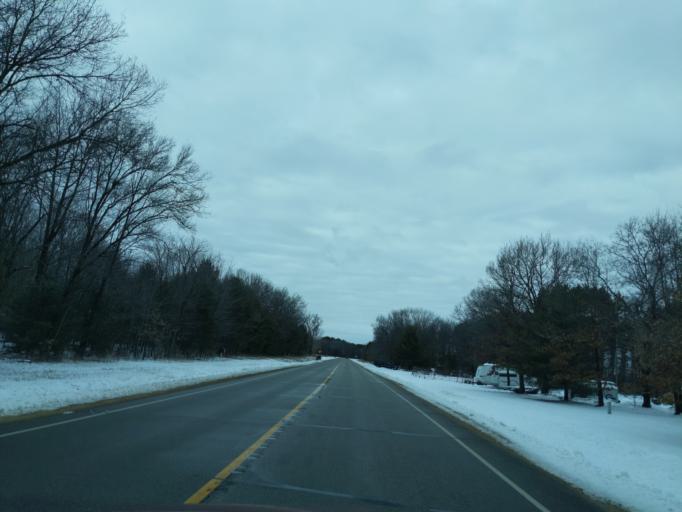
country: US
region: Wisconsin
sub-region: Waushara County
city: Wautoma
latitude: 43.9392
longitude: -89.3136
